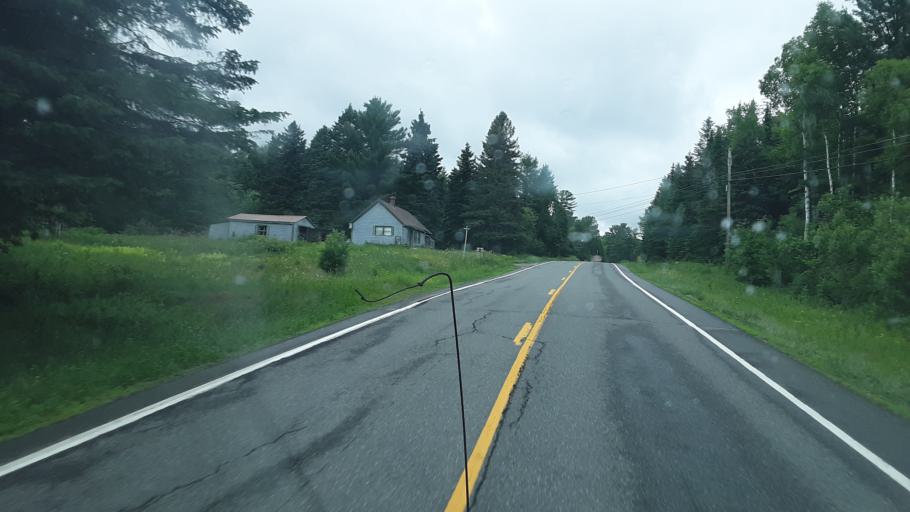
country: US
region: Maine
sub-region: Aroostook County
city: Presque Isle
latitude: 46.4748
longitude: -68.3884
